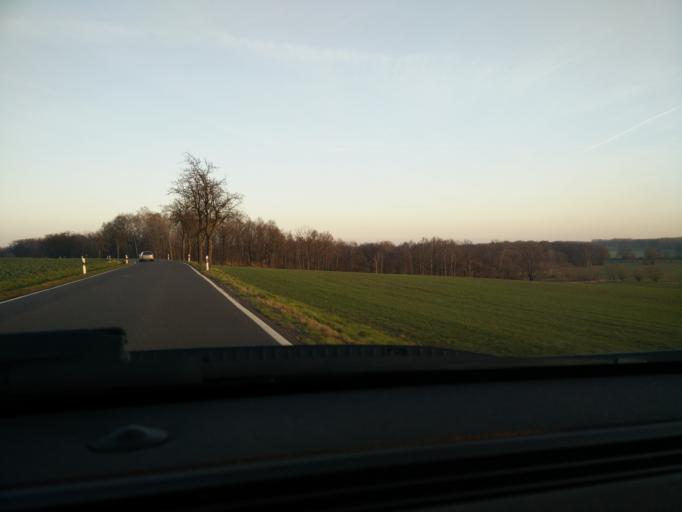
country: DE
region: Saxony
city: Kitzscher
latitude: 51.1500
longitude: 12.5944
